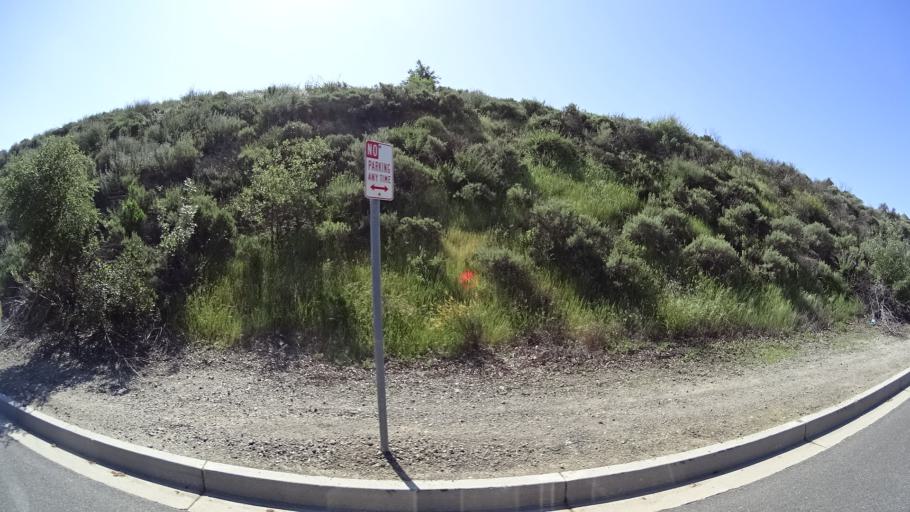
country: US
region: California
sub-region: Ventura County
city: Casa Conejo
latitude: 34.1735
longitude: -118.9312
